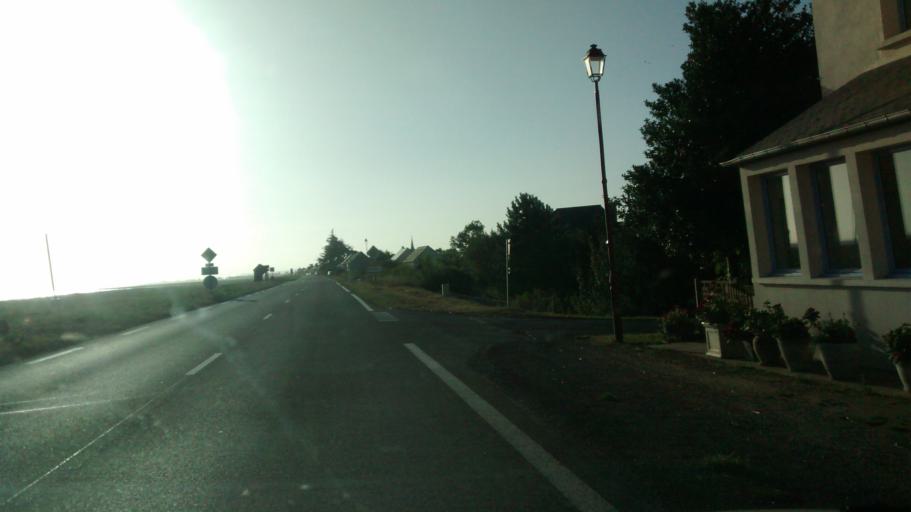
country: FR
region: Brittany
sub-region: Departement d'Ille-et-Vilaine
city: Hirel
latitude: 48.6082
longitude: -1.8129
